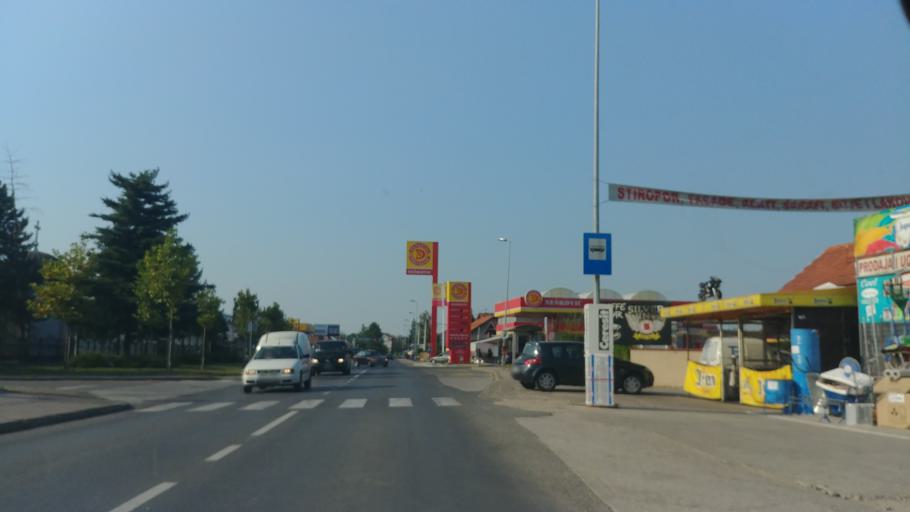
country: BA
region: Brcko
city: Brcko
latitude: 44.8608
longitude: 18.8122
